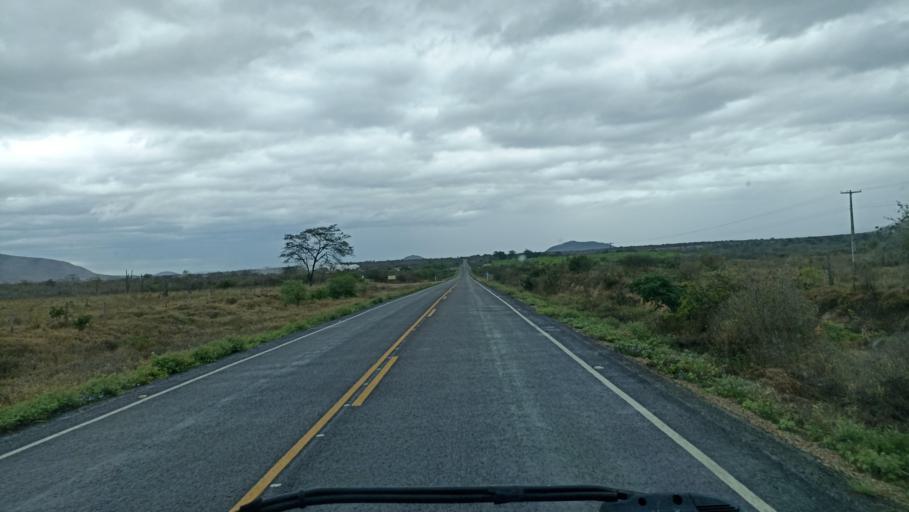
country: BR
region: Bahia
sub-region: Iacu
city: Iacu
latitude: -12.9690
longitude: -40.4965
